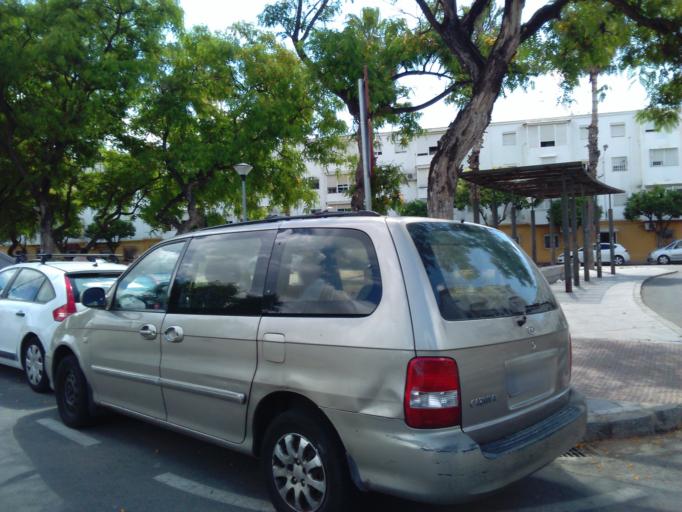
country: ES
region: Andalusia
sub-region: Provincia de Sevilla
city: La Algaba
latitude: 37.4293
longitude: -5.9824
